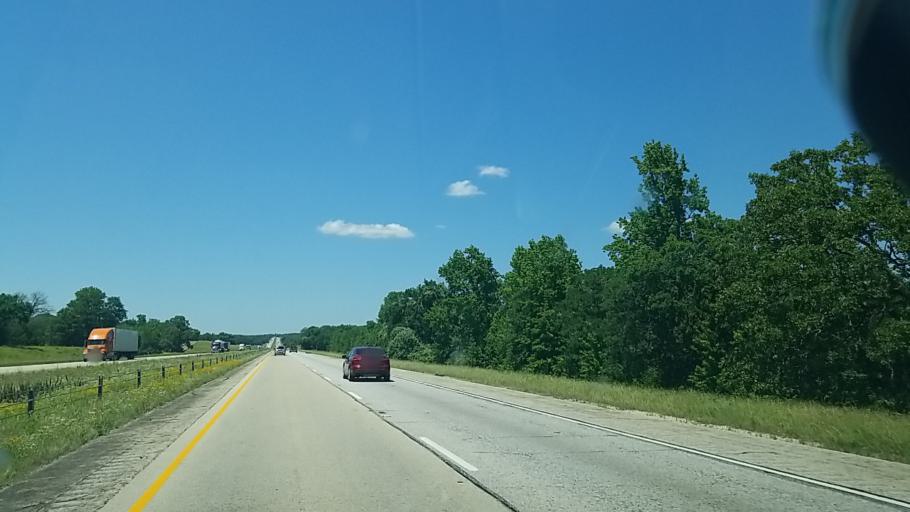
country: US
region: Texas
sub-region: Leon County
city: Centerville
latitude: 31.1724
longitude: -95.9882
